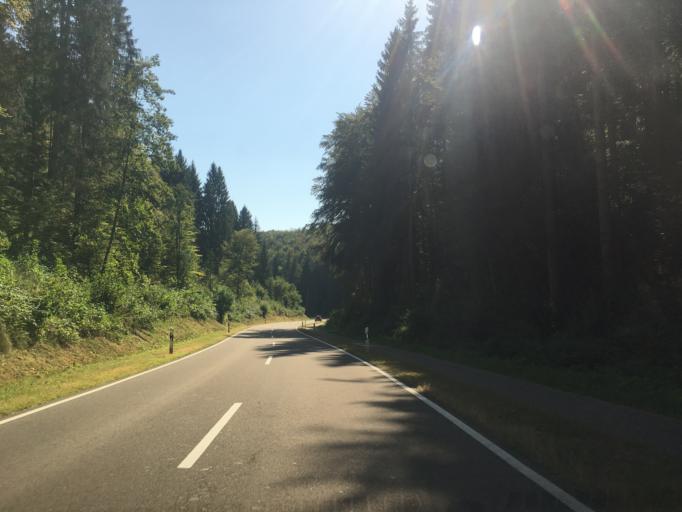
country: DE
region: Baden-Wuerttemberg
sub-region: Tuebingen Region
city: Munsingen
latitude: 48.3784
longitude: 9.4832
